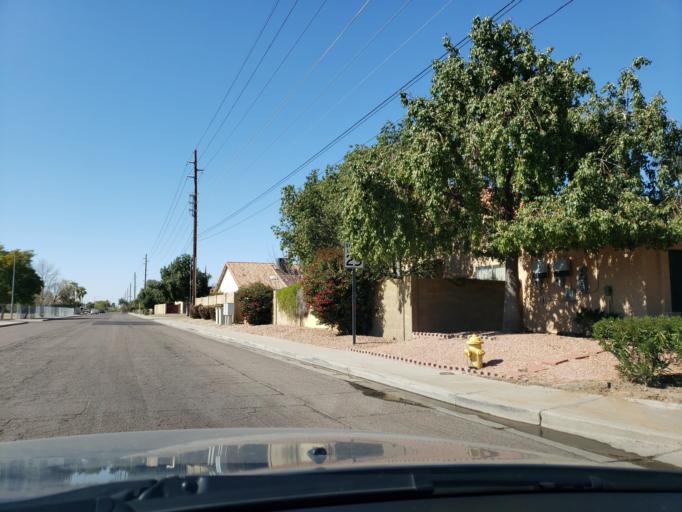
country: US
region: Arizona
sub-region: Maricopa County
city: Glendale
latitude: 33.6475
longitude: -112.0747
